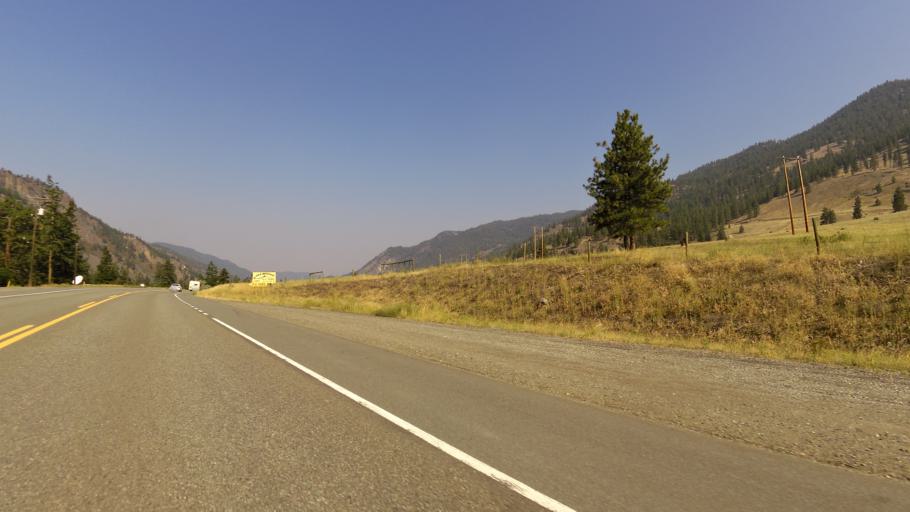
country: CA
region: British Columbia
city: Princeton
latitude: 49.3669
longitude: -120.1277
